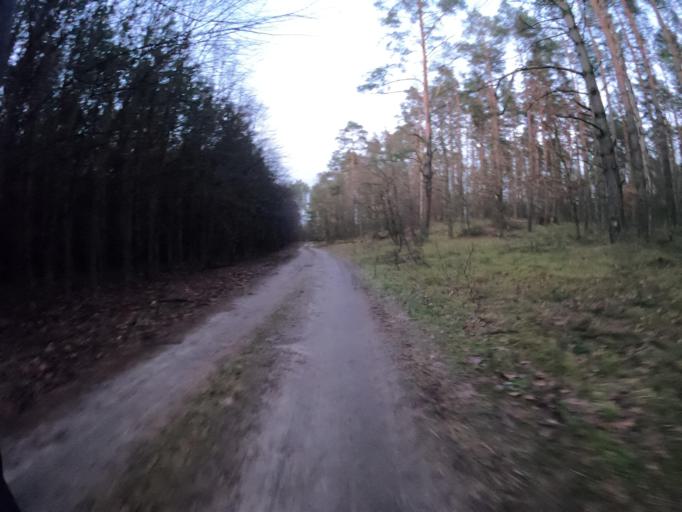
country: PL
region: Greater Poland Voivodeship
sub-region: Powiat zlotowski
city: Sypniewo
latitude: 53.4808
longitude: 16.6342
